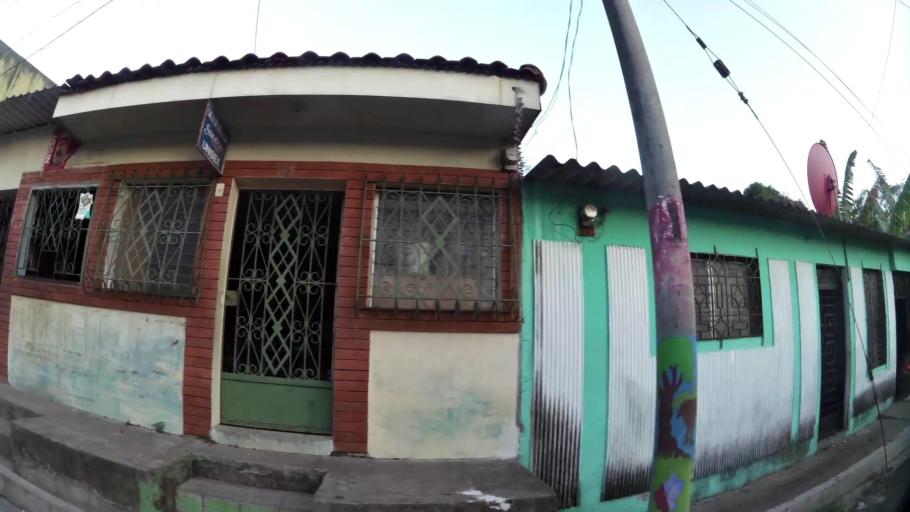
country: SV
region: Sonsonate
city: Armenia
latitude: 13.7336
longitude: -89.3834
